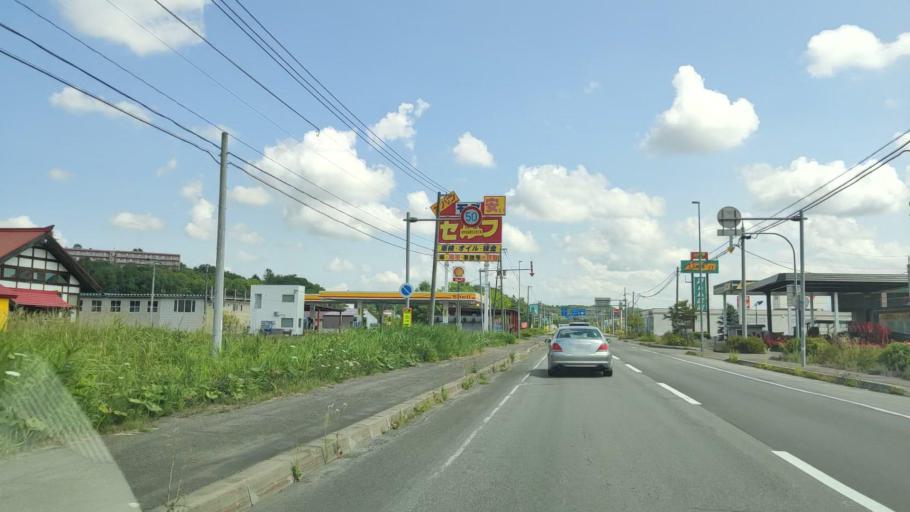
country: JP
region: Hokkaido
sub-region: Asahikawa-shi
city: Asahikawa
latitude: 43.5958
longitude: 142.4611
